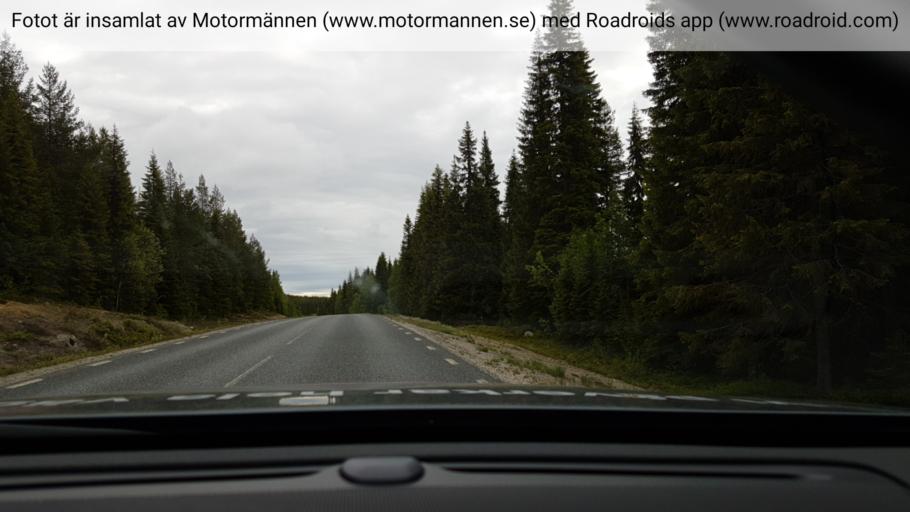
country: SE
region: Vaesterbotten
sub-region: Asele Kommun
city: Insjon
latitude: 64.3503
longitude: 17.8219
